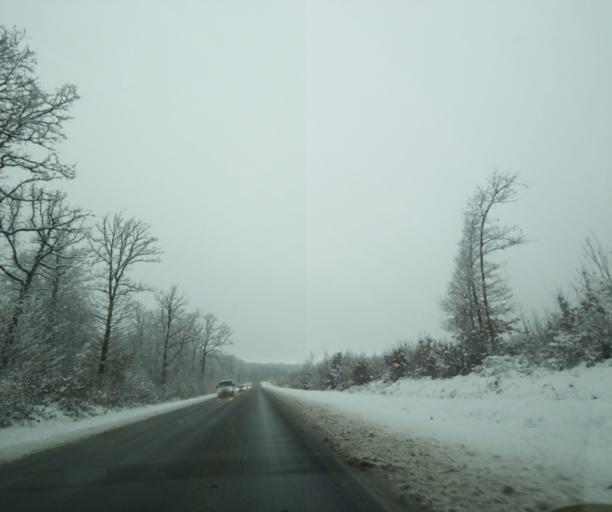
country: FR
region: Champagne-Ardenne
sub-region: Departement de la Haute-Marne
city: Laneuville-a-Remy
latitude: 48.5474
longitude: 4.8332
